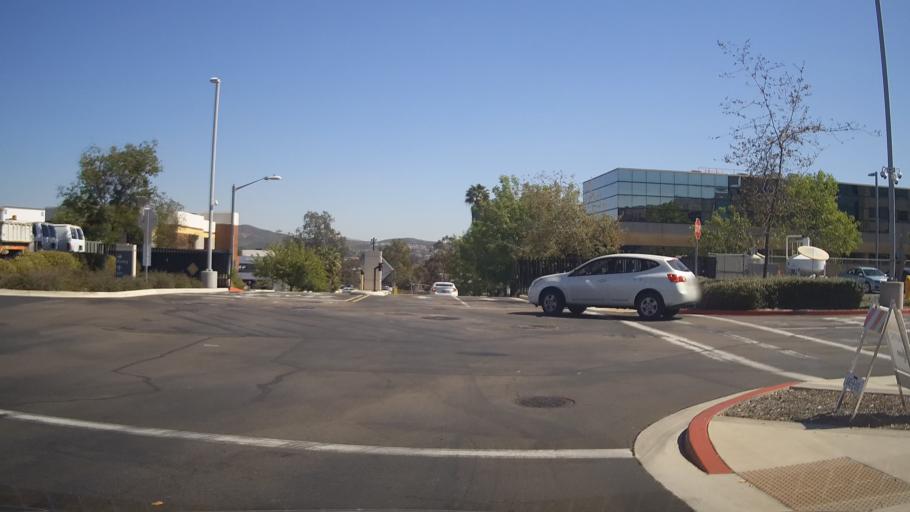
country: US
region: California
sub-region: San Diego County
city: San Diego
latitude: 32.8357
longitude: -117.1289
